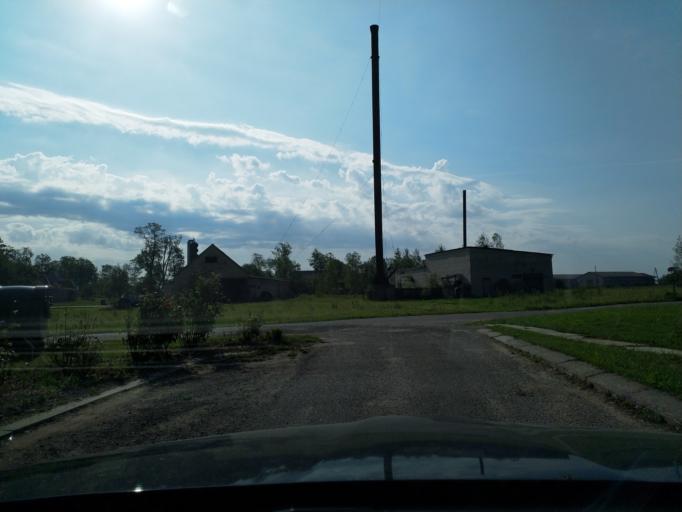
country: LV
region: Talsu Rajons
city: Sabile
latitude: 56.9492
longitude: 22.3963
